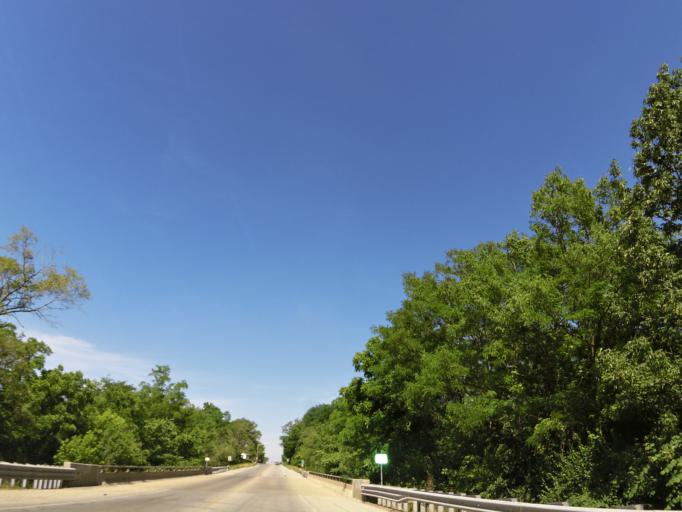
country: US
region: Illinois
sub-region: Vermilion County
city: Danville
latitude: 40.1324
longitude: -87.5739
